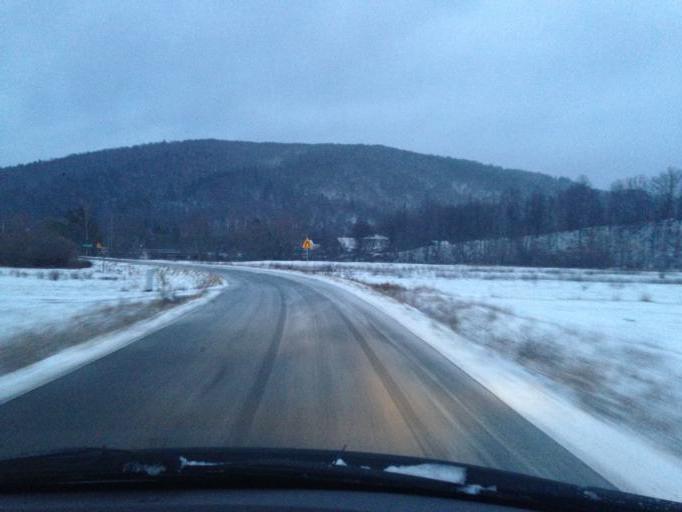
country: PL
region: Subcarpathian Voivodeship
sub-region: Powiat jasielski
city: Krempna
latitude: 49.5037
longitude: 21.5348
